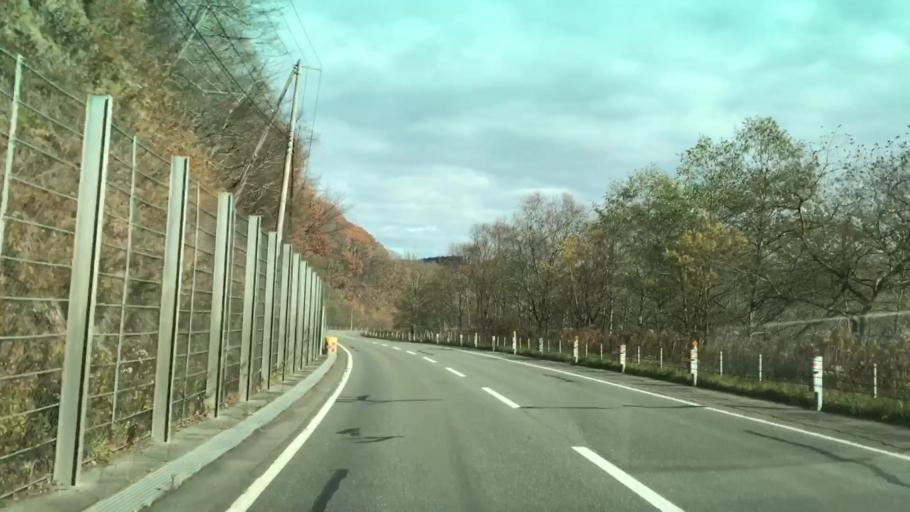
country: JP
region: Hokkaido
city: Shizunai-furukawacho
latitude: 42.7131
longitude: 142.2477
